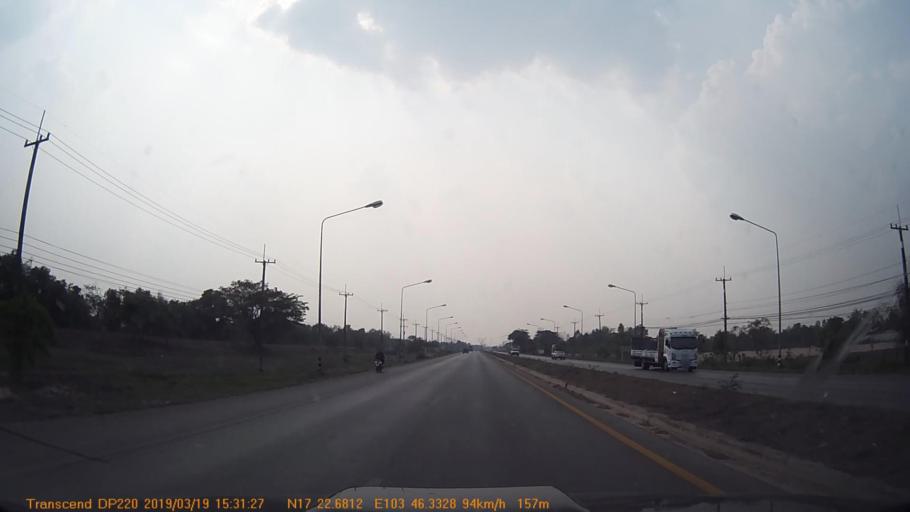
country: TH
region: Sakon Nakhon
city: Phang Khon
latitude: 17.3781
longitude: 103.7716
